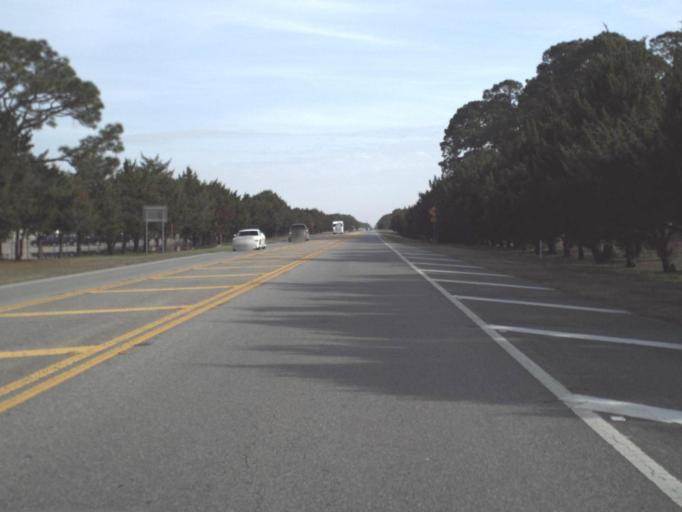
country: US
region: Florida
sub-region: Bay County
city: Tyndall Air Force Base
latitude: 30.0691
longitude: -85.5892
